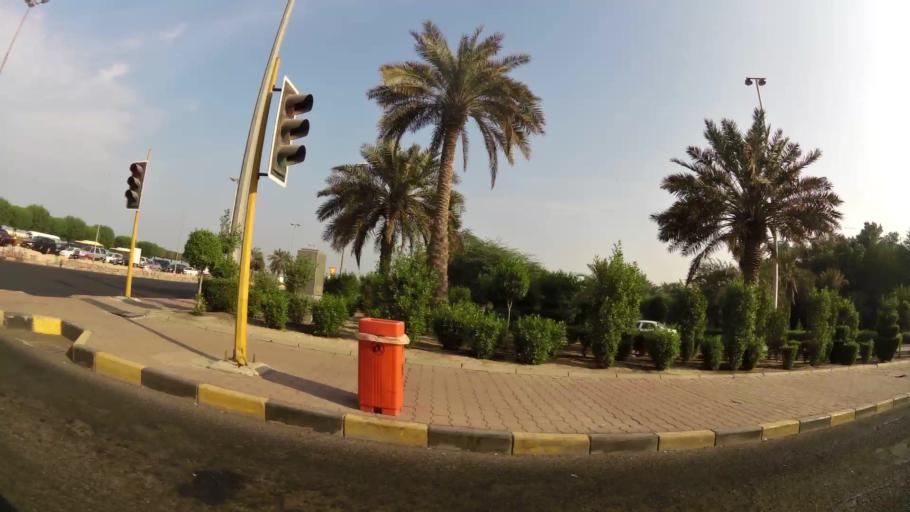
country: KW
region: Al Asimah
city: Ad Dasmah
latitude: 29.3687
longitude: 48.0129
